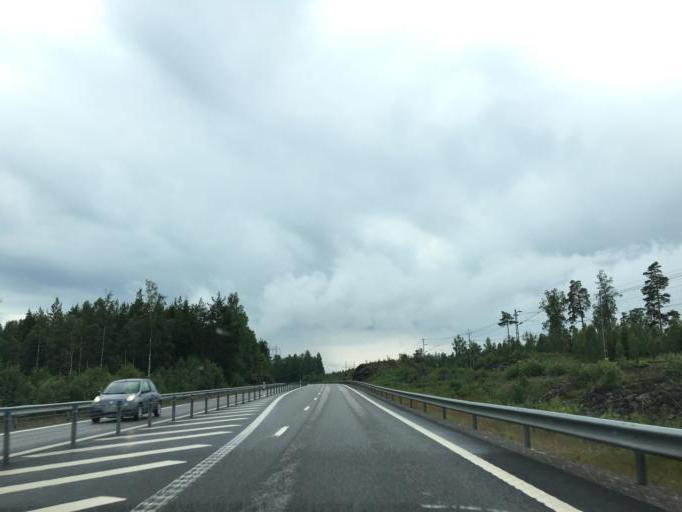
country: SE
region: OEstergoetland
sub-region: Norrkopings Kommun
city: Jursla
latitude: 58.8107
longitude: 16.1525
